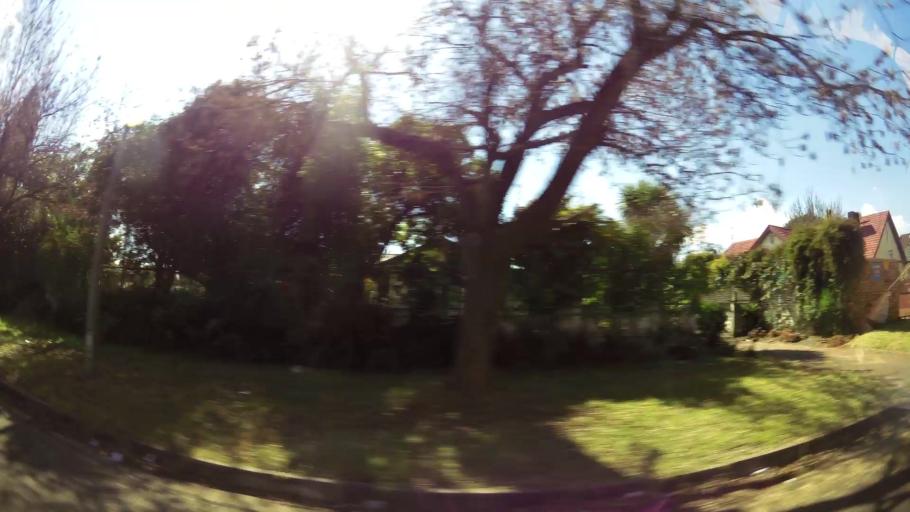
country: ZA
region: Mpumalanga
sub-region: Nkangala District Municipality
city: Witbank
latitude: -25.8849
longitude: 29.2199
